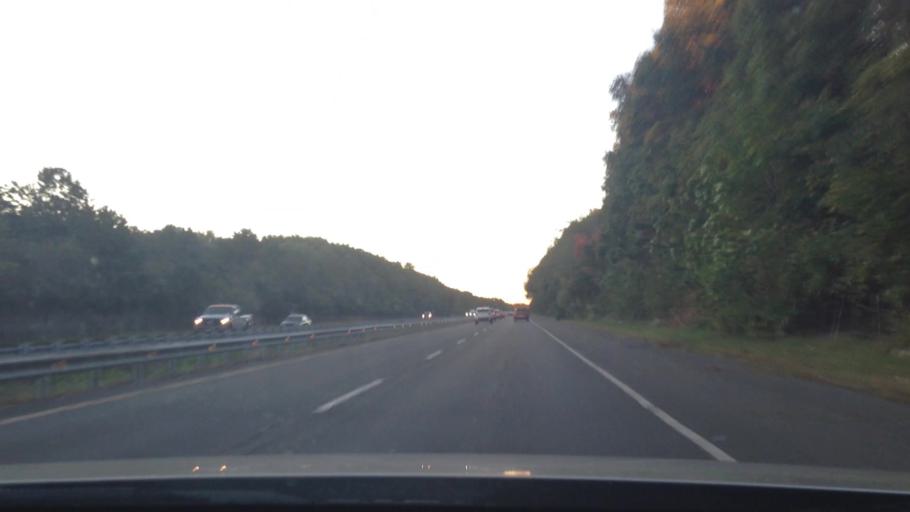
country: US
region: New York
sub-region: Suffolk County
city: Coram
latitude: 40.9063
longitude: -73.0056
